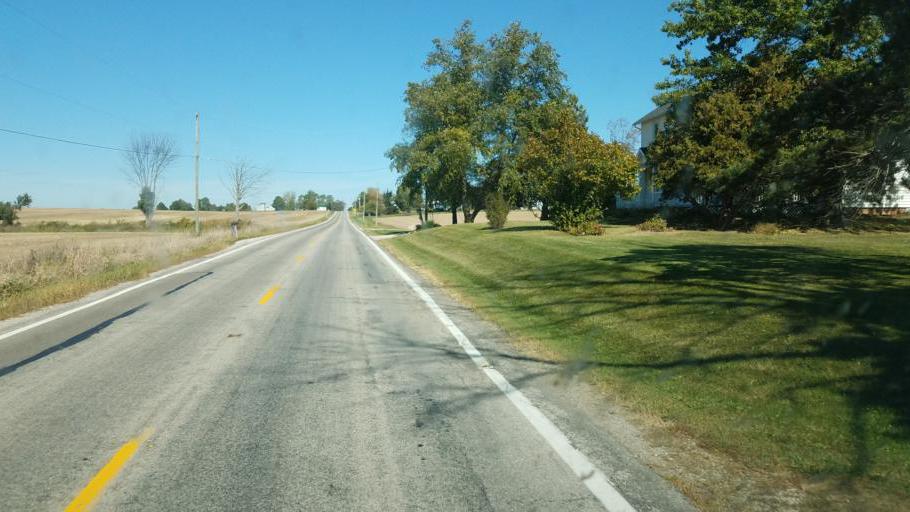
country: US
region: Ohio
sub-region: Crawford County
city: Bucyrus
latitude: 40.8984
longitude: -83.0167
